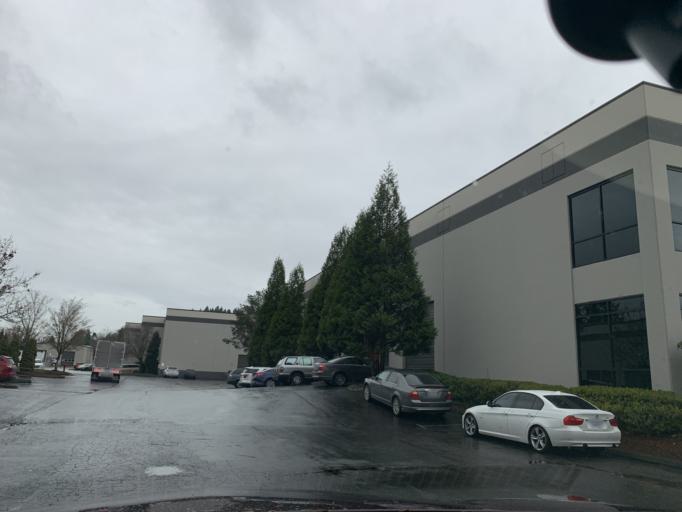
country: US
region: Washington
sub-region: King County
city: Woodinville
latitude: 47.7412
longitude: -122.1545
